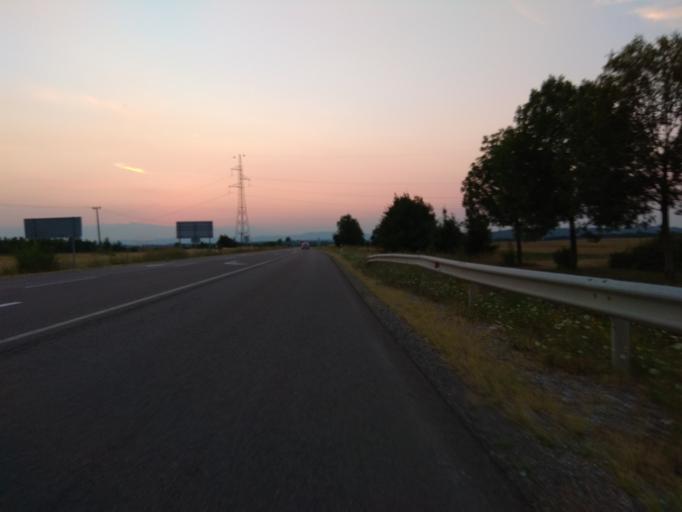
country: HU
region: Borsod-Abauj-Zemplen
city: Emod
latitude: 47.9236
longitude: 20.8400
